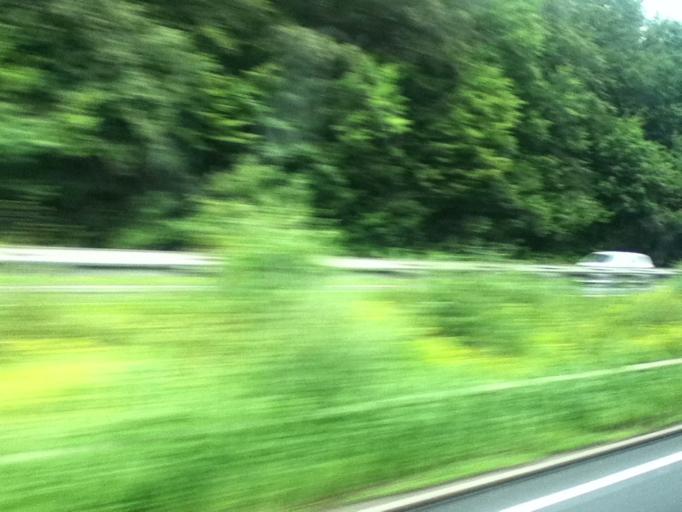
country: DE
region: Hesse
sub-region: Regierungsbezirk Kassel
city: Bad Hersfeld
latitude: 50.8552
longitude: 9.7472
